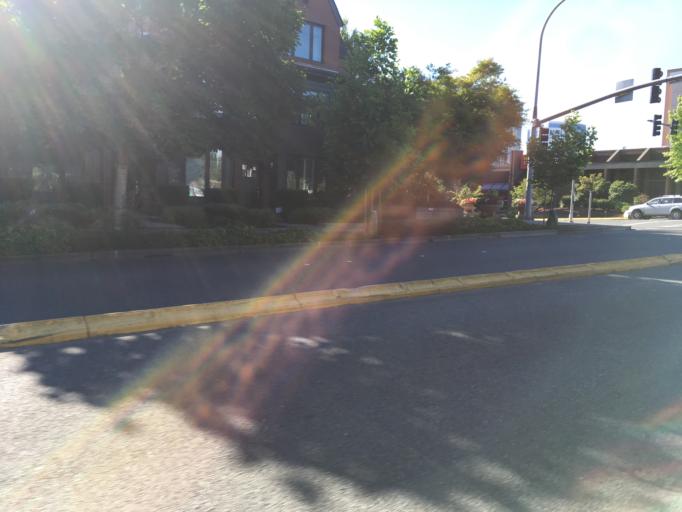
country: US
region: Washington
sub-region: King County
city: Bellevue
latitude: 47.6216
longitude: -122.2018
